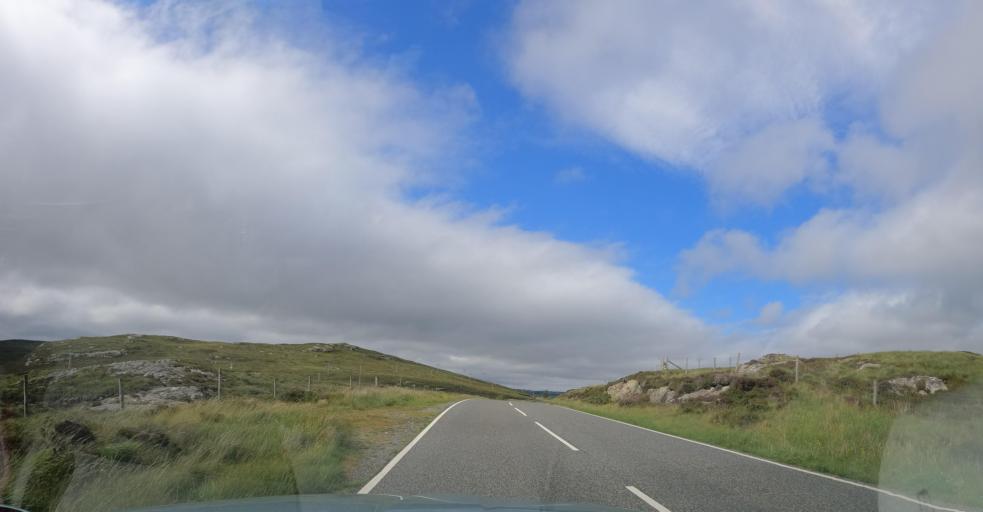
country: GB
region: Scotland
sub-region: Eilean Siar
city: Stornoway
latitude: 58.1252
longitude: -6.5074
